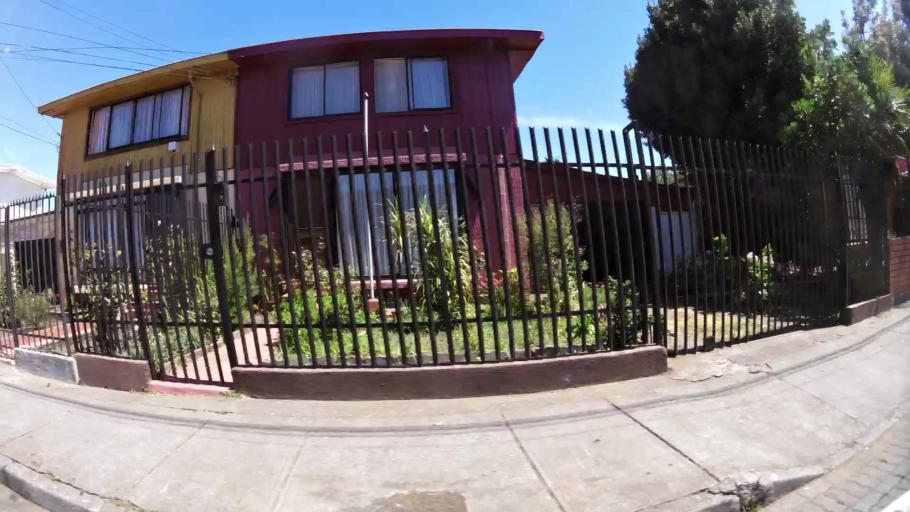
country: CL
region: Biobio
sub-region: Provincia de Concepcion
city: Talcahuano
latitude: -36.7551
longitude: -73.0905
